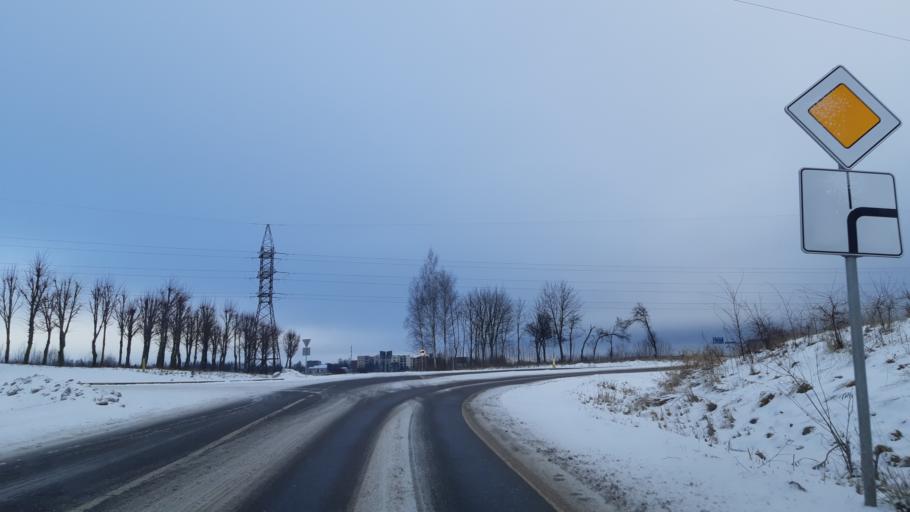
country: LT
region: Kauno apskritis
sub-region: Kaunas
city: Silainiai
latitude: 54.9377
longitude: 23.8731
